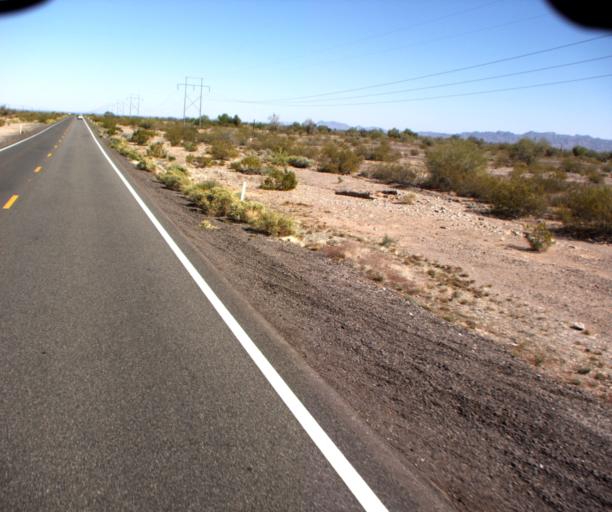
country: US
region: Arizona
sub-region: La Paz County
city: Quartzsite
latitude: 33.5961
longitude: -114.2170
